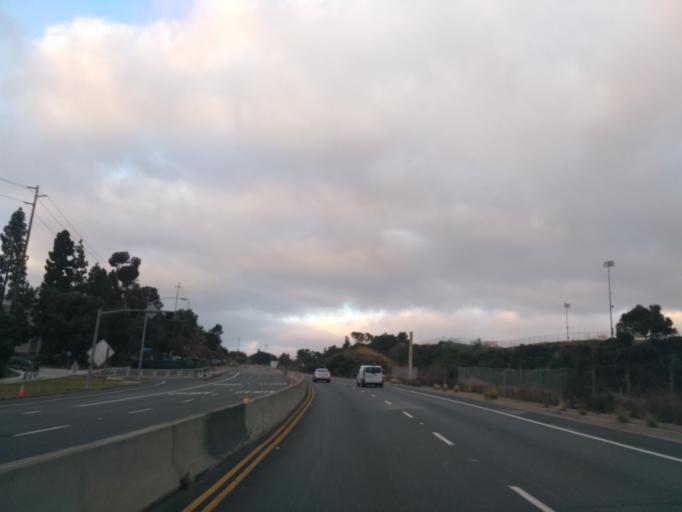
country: US
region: California
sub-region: San Diego County
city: La Jolla
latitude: 32.8084
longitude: -117.2089
